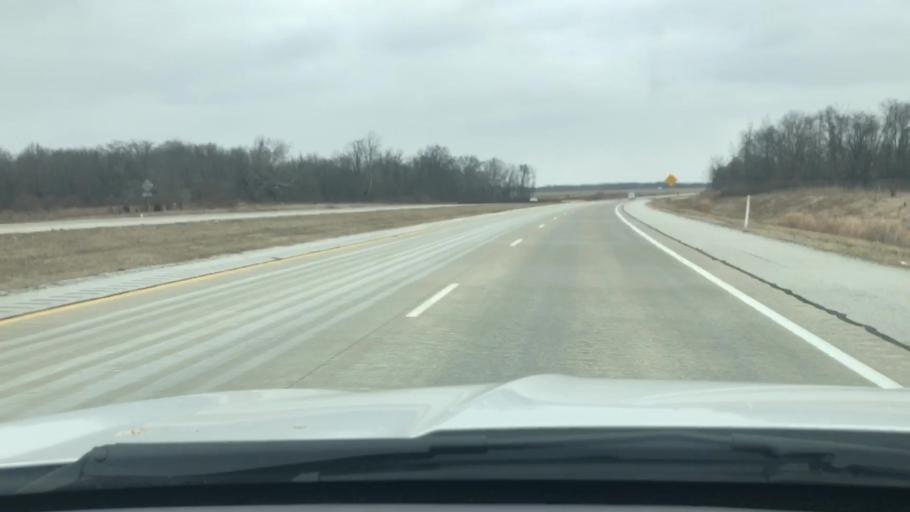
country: US
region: Indiana
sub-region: Tippecanoe County
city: Battle Ground
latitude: 40.4872
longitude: -86.7712
